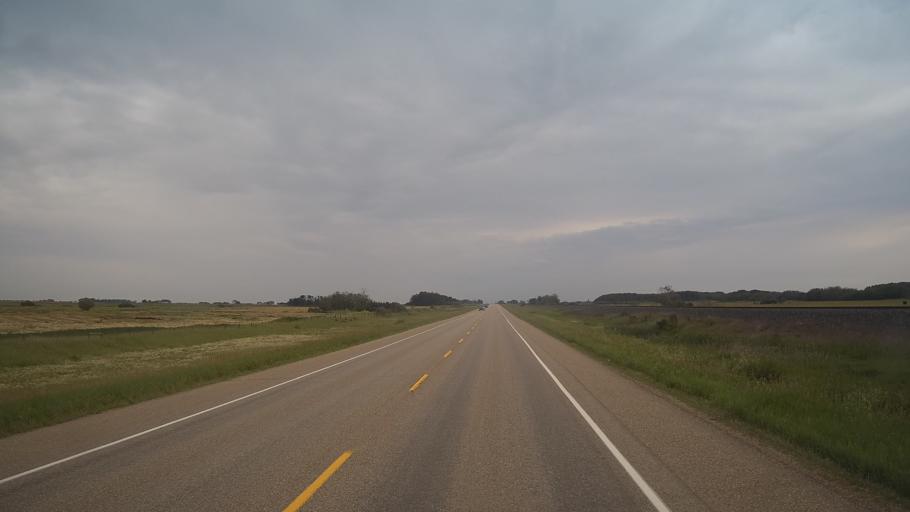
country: CA
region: Saskatchewan
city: Langham
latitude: 52.1270
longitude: -107.2665
